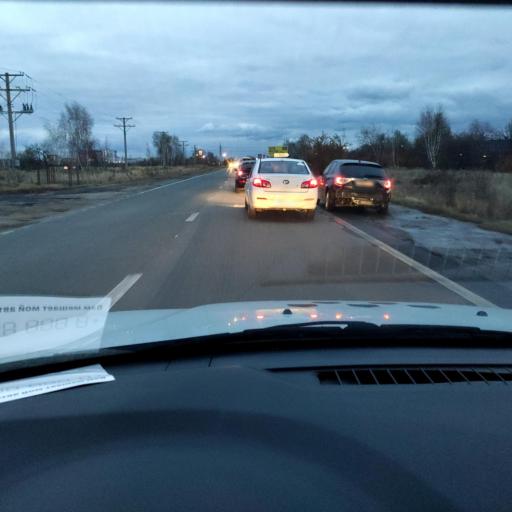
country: RU
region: Samara
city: Tol'yatti
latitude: 53.5494
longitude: 49.3740
